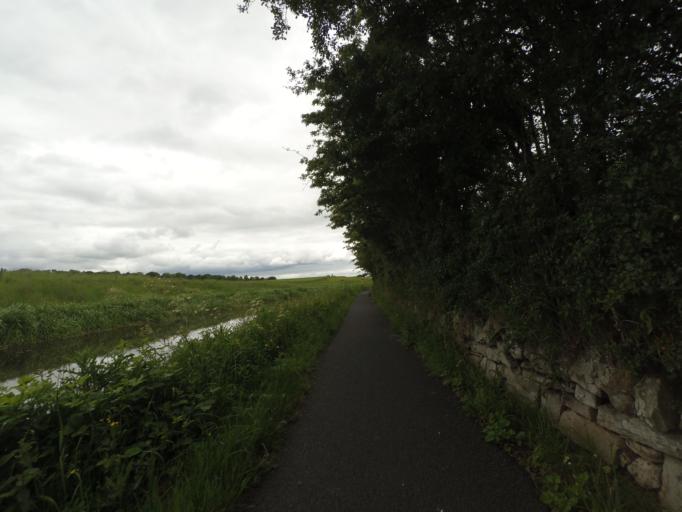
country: GB
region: Scotland
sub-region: West Lothian
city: Linlithgow
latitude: 55.9754
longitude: -3.5352
